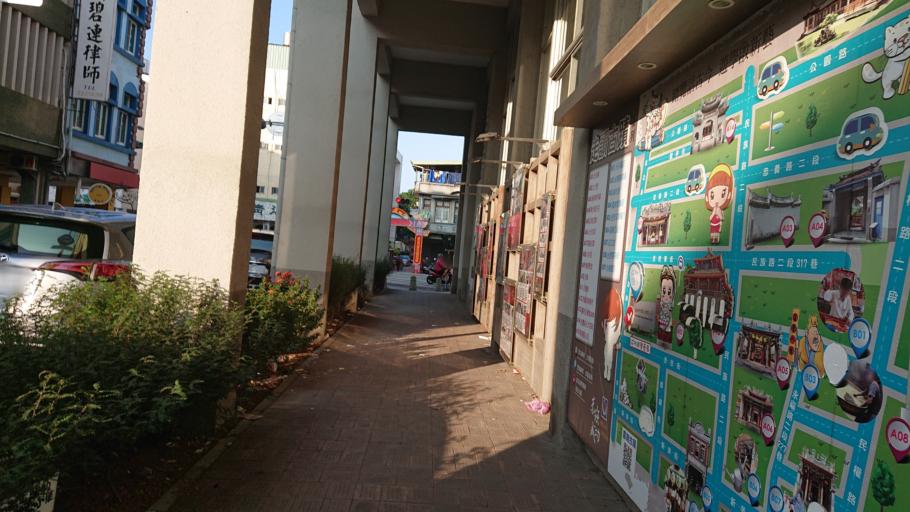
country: TW
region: Taiwan
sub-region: Tainan
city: Tainan
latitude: 22.9988
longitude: 120.2027
